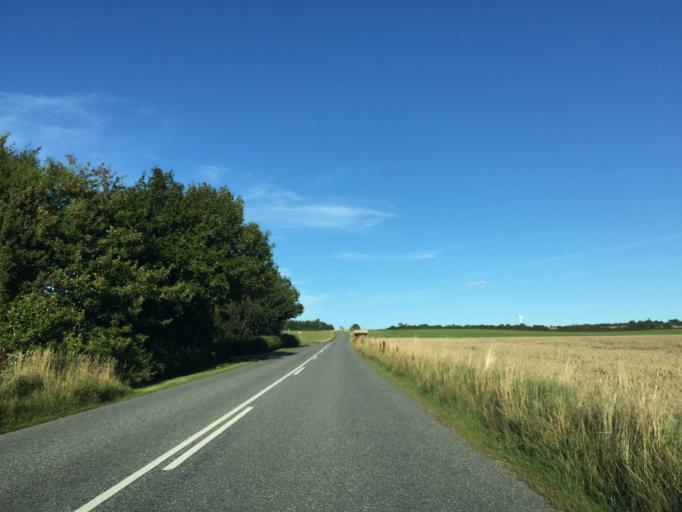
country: DK
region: Central Jutland
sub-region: Silkeborg Kommune
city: Svejbaek
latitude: 56.2478
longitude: 9.6925
